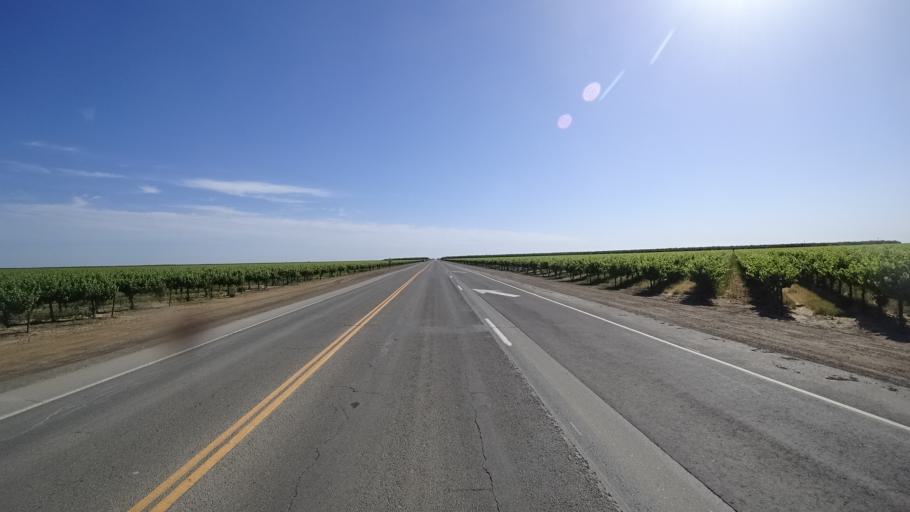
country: US
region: California
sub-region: Fresno County
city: Huron
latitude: 36.1394
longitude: -120.0093
